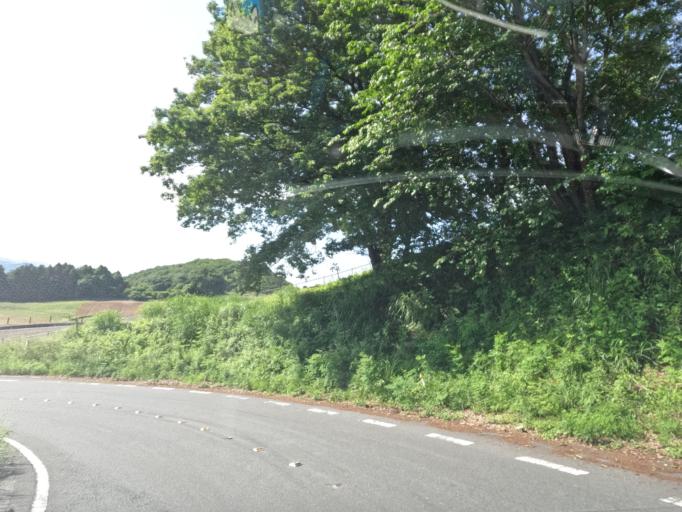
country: JP
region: Saitama
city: Yorii
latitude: 36.0497
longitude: 139.1511
